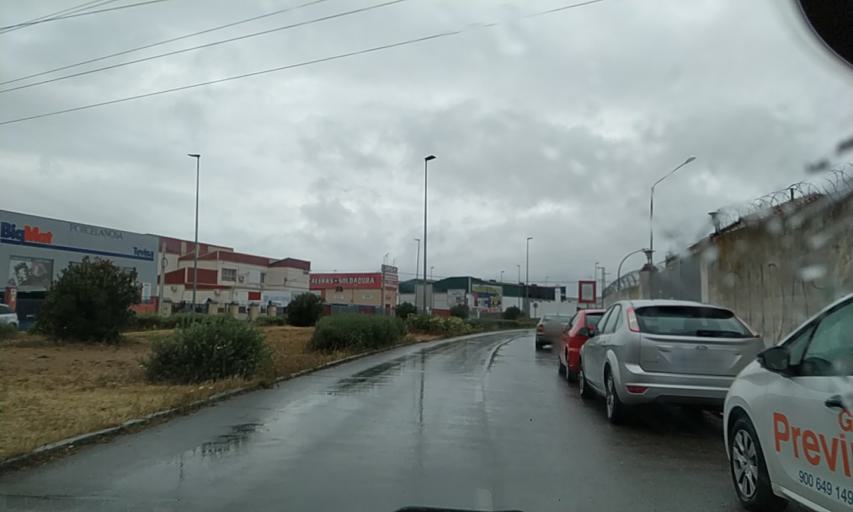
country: ES
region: Extremadura
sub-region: Provincia de Badajoz
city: Badajoz
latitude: 38.8890
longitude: -6.9924
